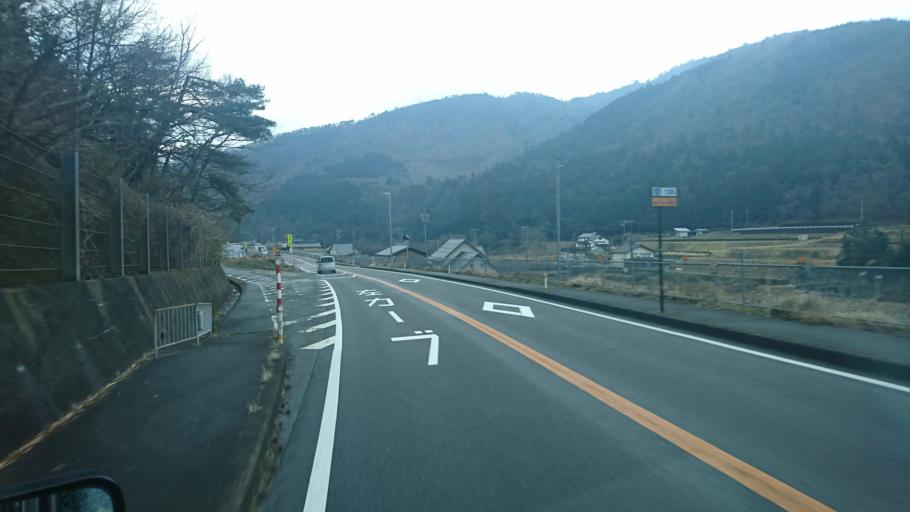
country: JP
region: Hyogo
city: Toyooka
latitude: 35.3809
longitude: 134.6645
